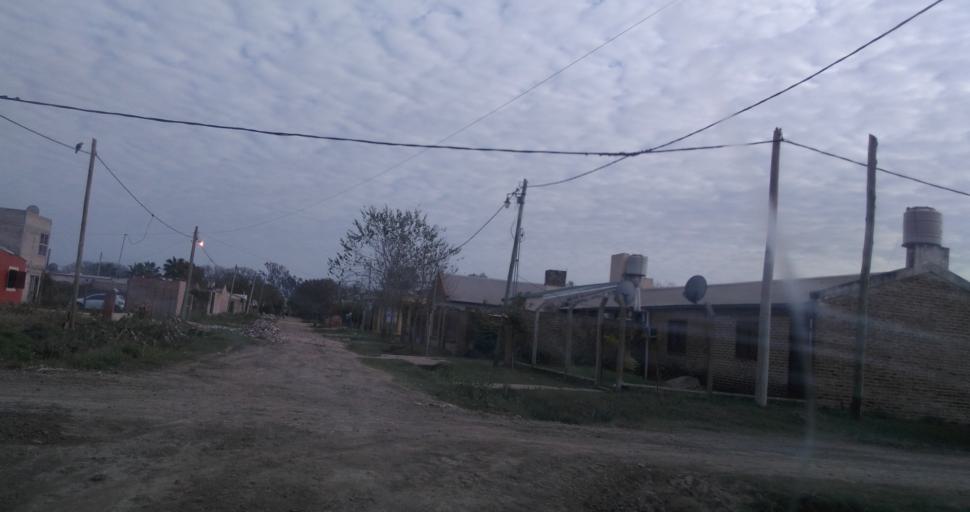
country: AR
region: Chaco
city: Fontana
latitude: -27.4457
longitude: -59.0329
